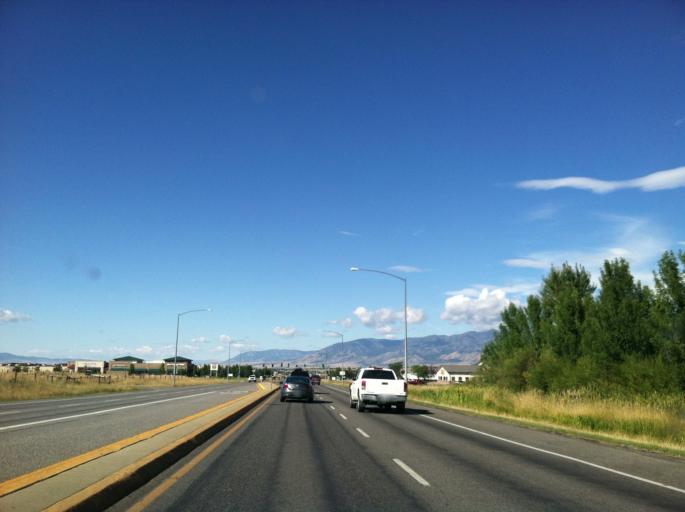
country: US
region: Montana
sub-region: Gallatin County
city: Bozeman
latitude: 45.7047
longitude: -111.0650
